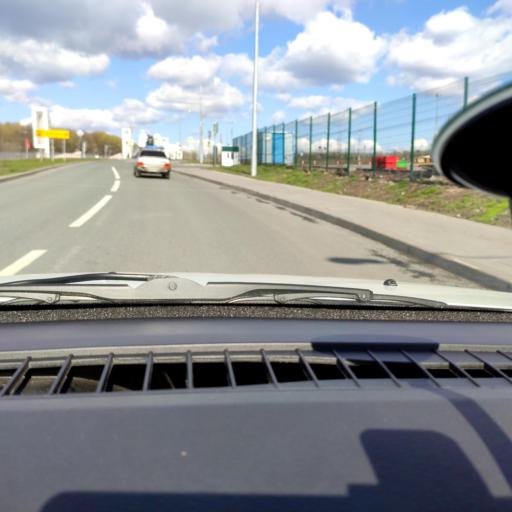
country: RU
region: Samara
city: Petra-Dubrava
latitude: 53.2736
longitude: 50.2545
